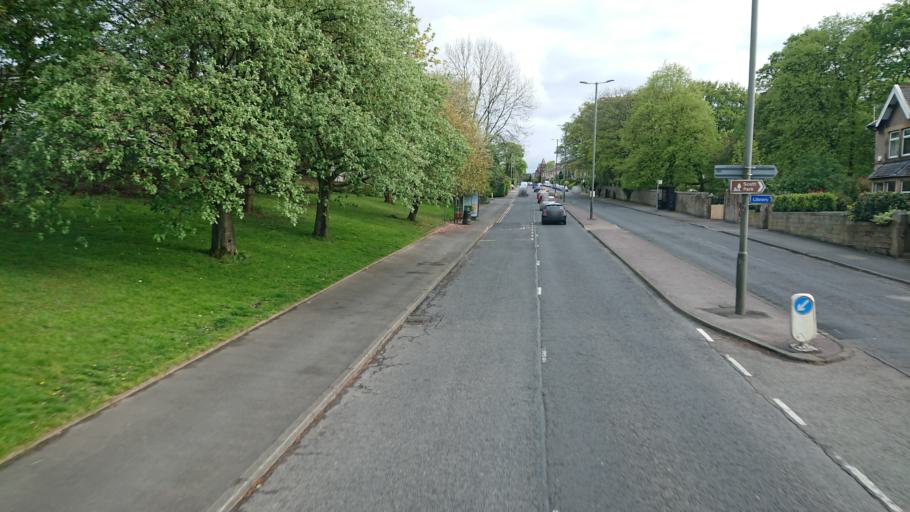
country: GB
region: England
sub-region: Lancashire
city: Burnley
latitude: 53.7824
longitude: -2.2536
